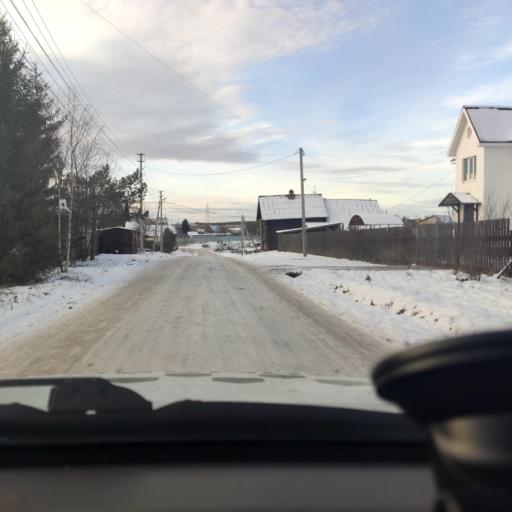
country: RU
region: Perm
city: Ferma
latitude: 57.9410
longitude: 56.3500
